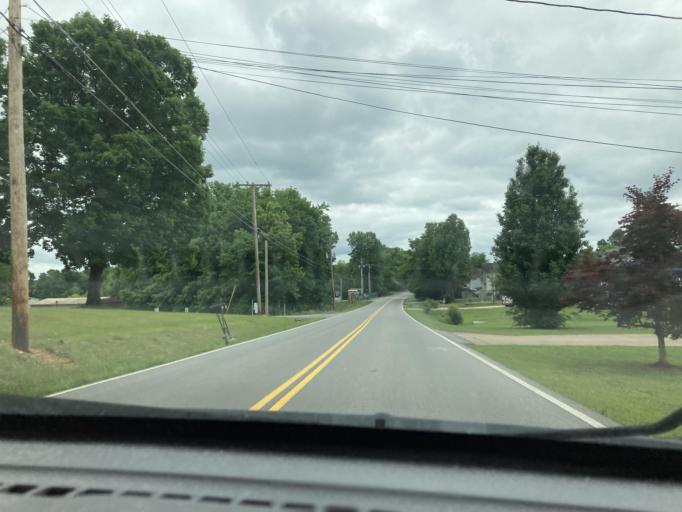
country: US
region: Tennessee
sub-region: Dickson County
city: Dickson
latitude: 36.0506
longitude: -87.3680
